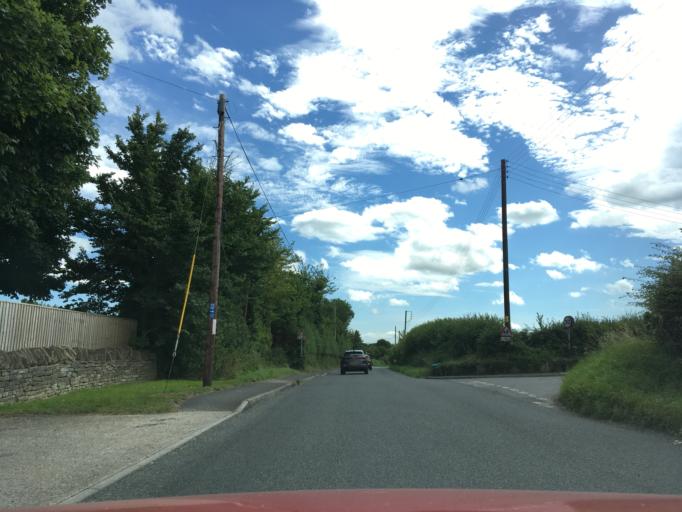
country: GB
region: England
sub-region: Somerset
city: Ilchester
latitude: 51.0532
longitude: -2.6697
